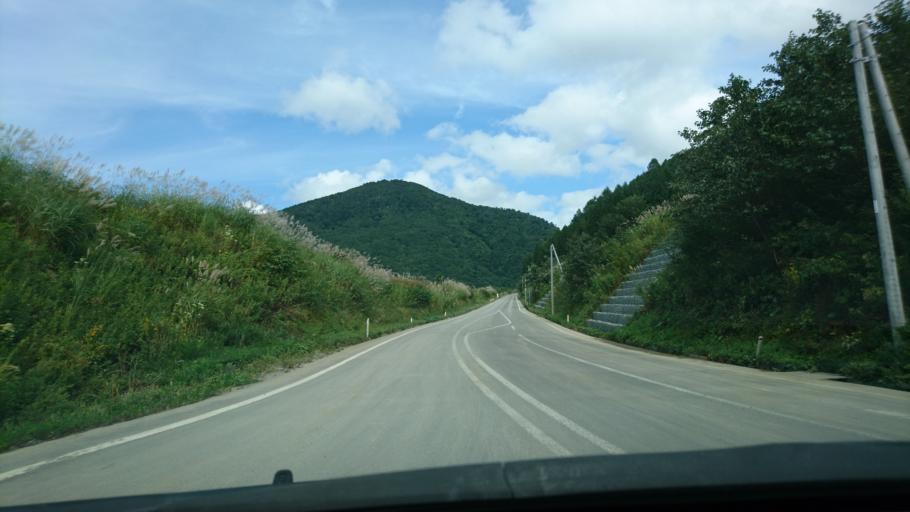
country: JP
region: Akita
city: Yuzawa
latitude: 39.0306
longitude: 140.7277
